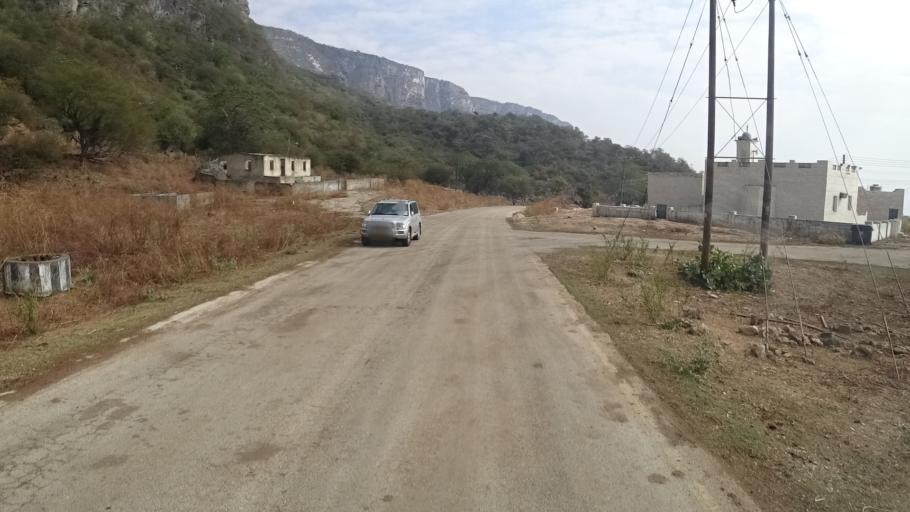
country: YE
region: Al Mahrah
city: Hawf
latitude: 16.7067
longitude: 53.2155
